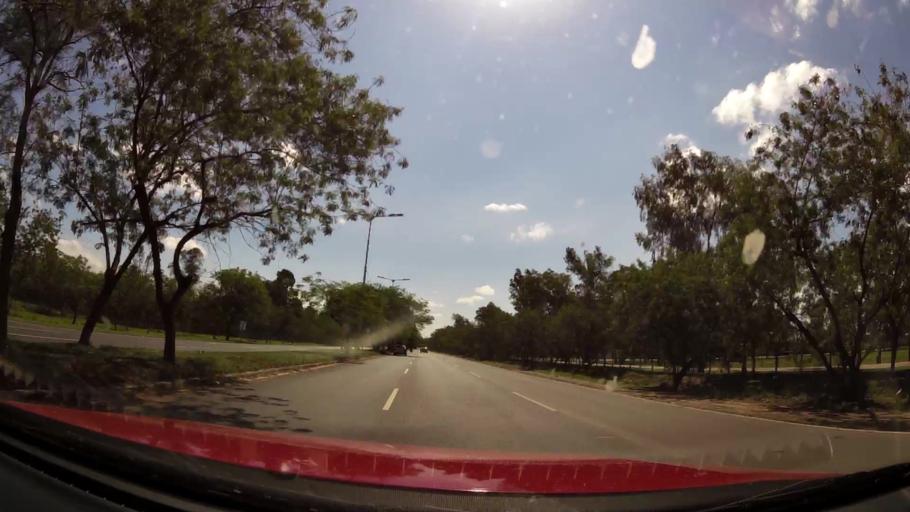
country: PY
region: Central
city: Fernando de la Mora
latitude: -25.2629
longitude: -57.5240
